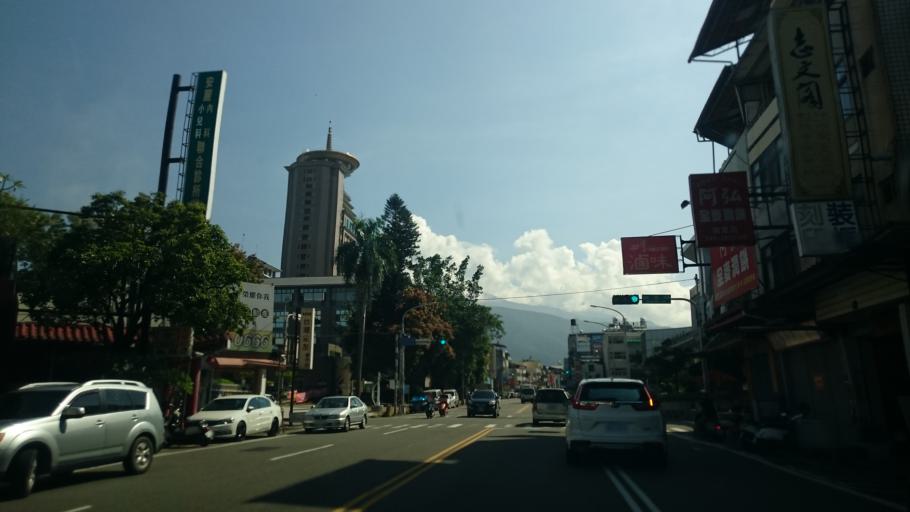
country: TW
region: Taiwan
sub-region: Nantou
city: Puli
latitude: 23.9663
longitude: 120.9687
